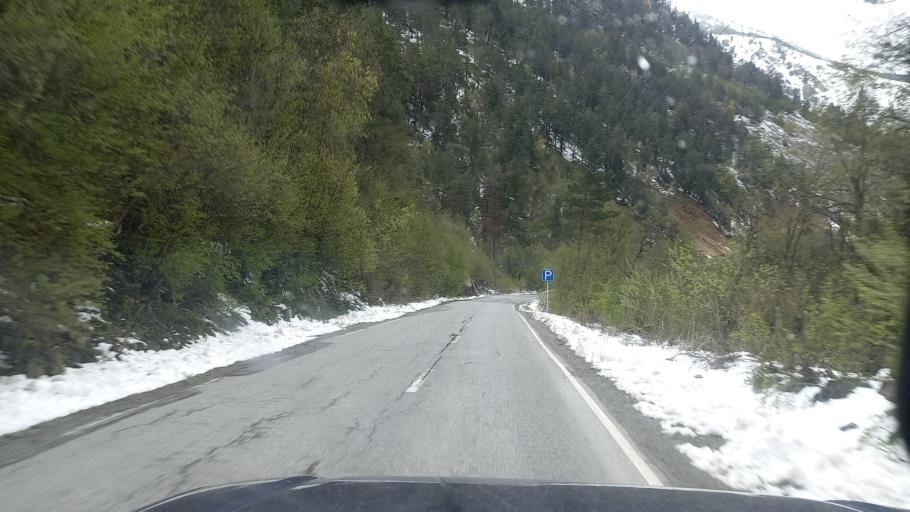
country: RU
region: North Ossetia
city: Mizur
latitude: 42.7962
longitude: 43.9254
